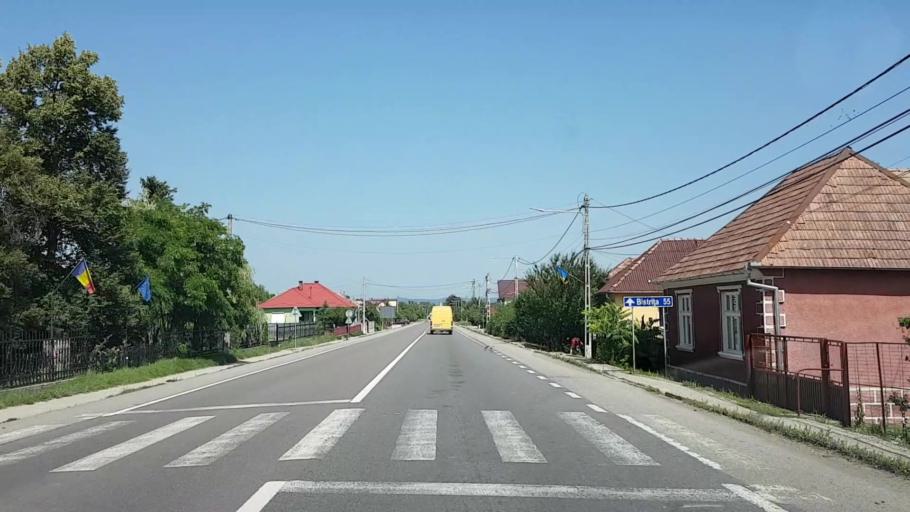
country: RO
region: Bistrita-Nasaud
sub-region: Comuna Ciceu-Mihaiesti
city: Ciceu-Mihaiesti
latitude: 47.1854
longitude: 23.9736
